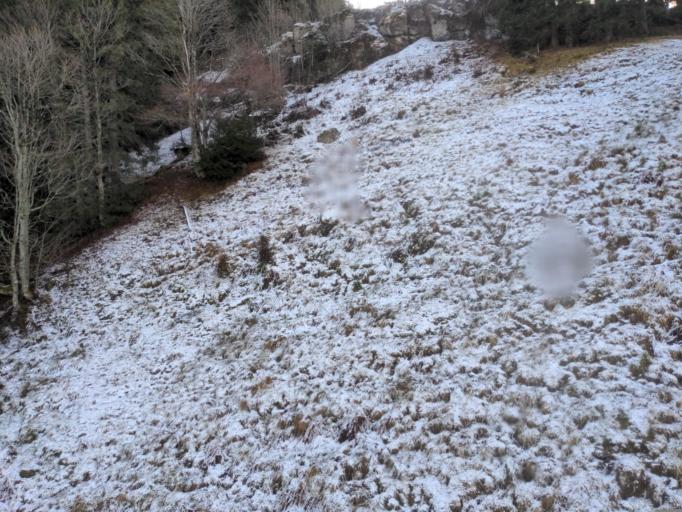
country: DE
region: Bavaria
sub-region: Swabia
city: Balderschwang
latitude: 47.5013
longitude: 10.0650
